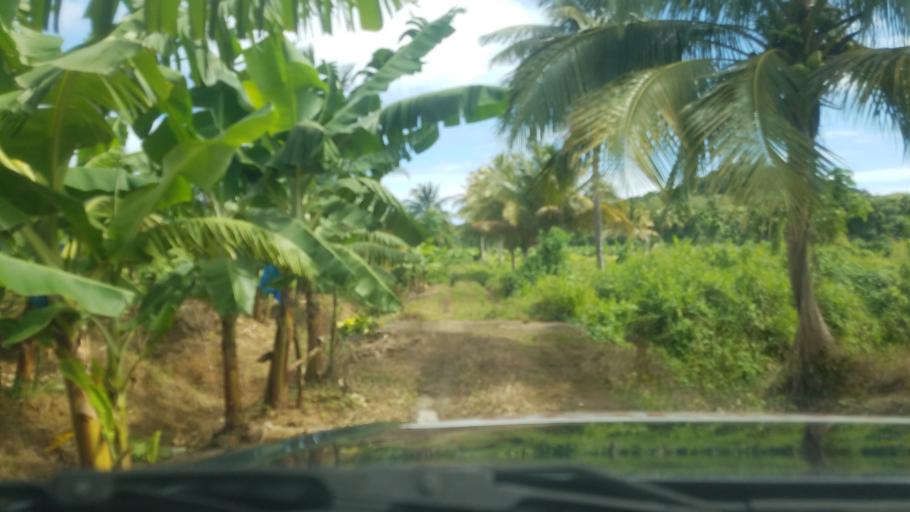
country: LC
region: Dennery Quarter
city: Dennery
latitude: 13.9342
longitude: -60.9191
